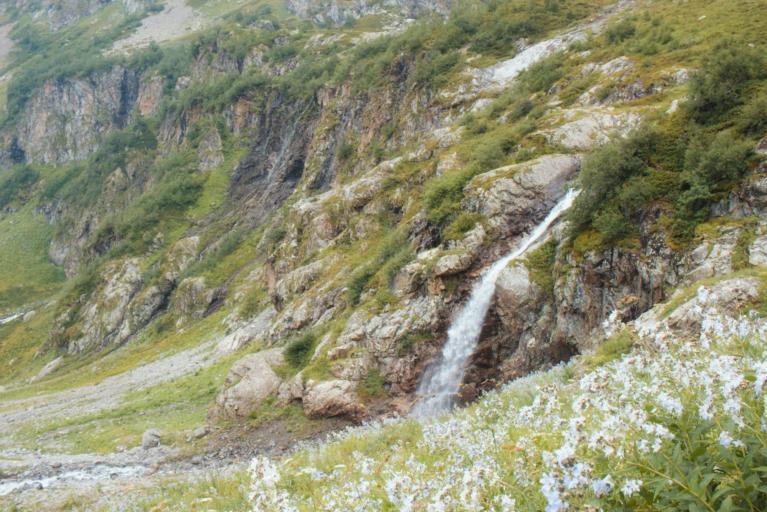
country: RU
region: Karachayevo-Cherkesiya
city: Nizhniy Arkhyz
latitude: 43.4431
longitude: 41.2509
